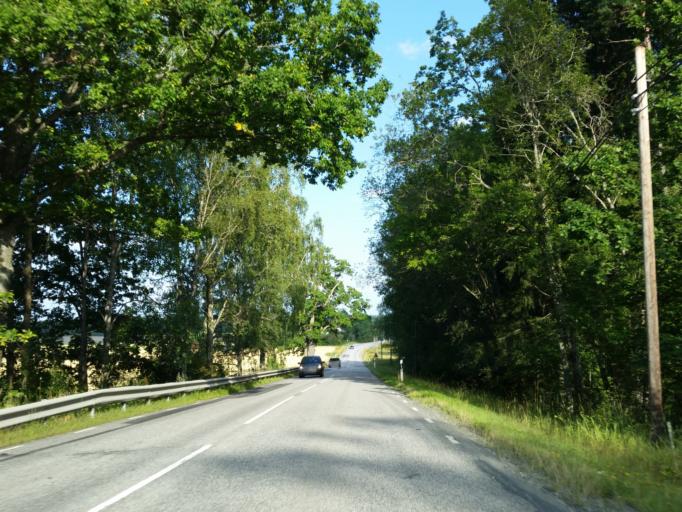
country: SE
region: Stockholm
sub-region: Nykvarns Kommun
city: Nykvarn
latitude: 59.2058
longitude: 17.3922
